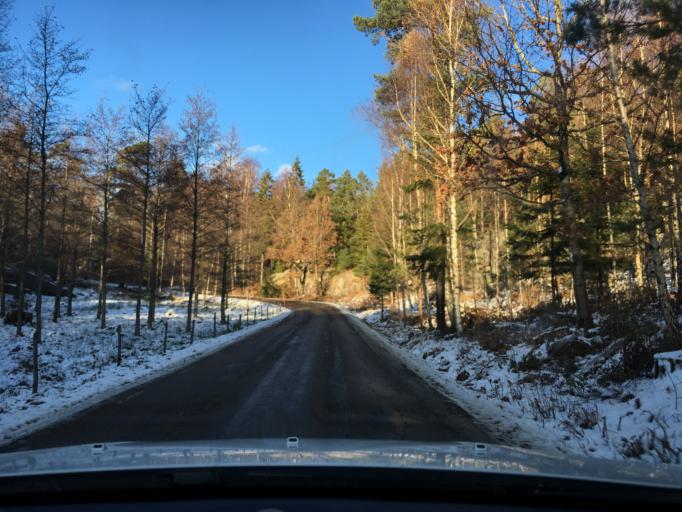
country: SE
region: Vaestra Goetaland
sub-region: Tjorns Kommun
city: Myggenas
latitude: 58.0911
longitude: 11.7492
